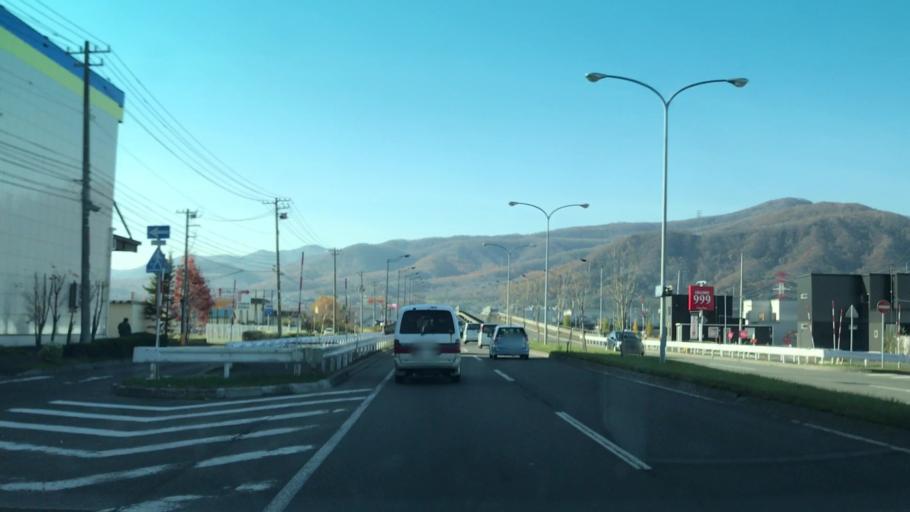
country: JP
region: Hokkaido
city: Sapporo
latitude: 43.1058
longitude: 141.2742
